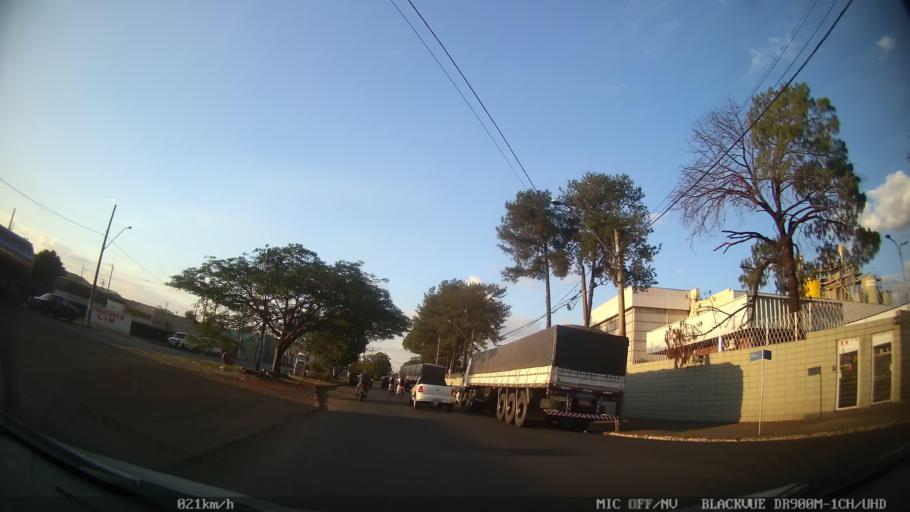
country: BR
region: Sao Paulo
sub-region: Ribeirao Preto
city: Ribeirao Preto
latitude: -21.1446
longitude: -47.7847
